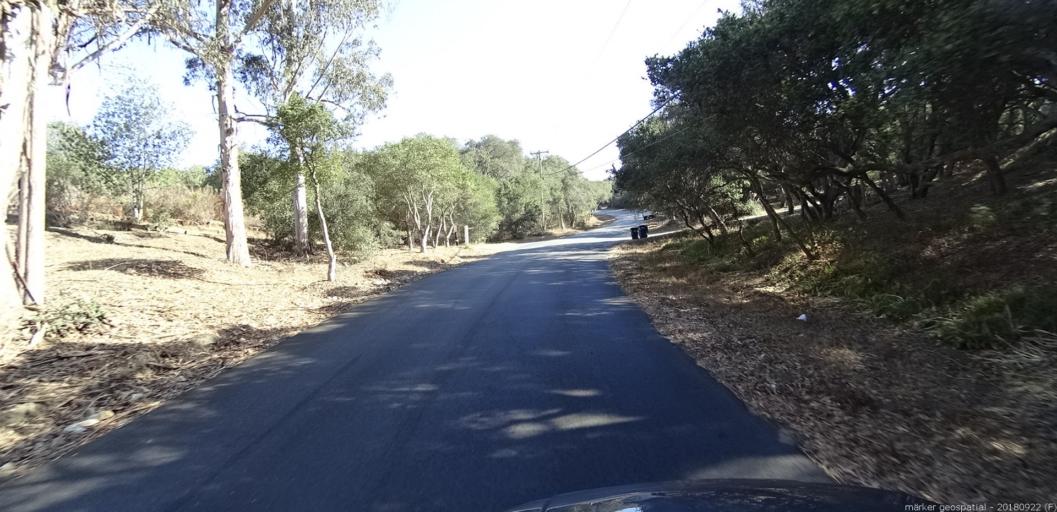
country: US
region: California
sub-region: Monterey County
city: Prunedale
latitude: 36.8240
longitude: -121.6421
